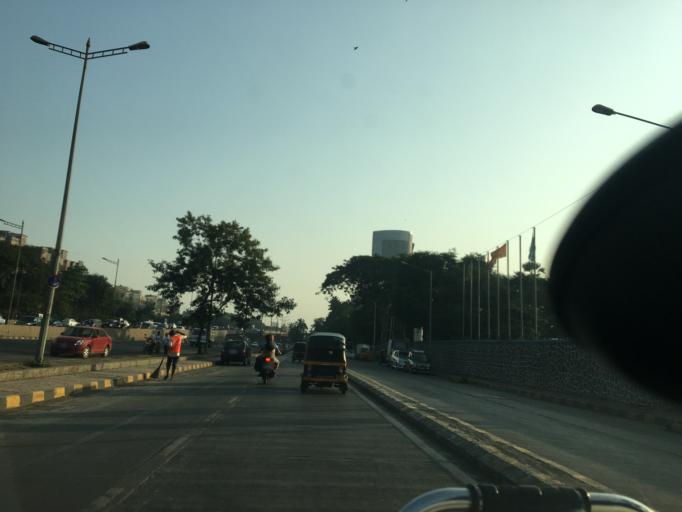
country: IN
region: Maharashtra
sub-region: Mumbai Suburban
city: Powai
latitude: 19.1487
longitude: 72.8560
